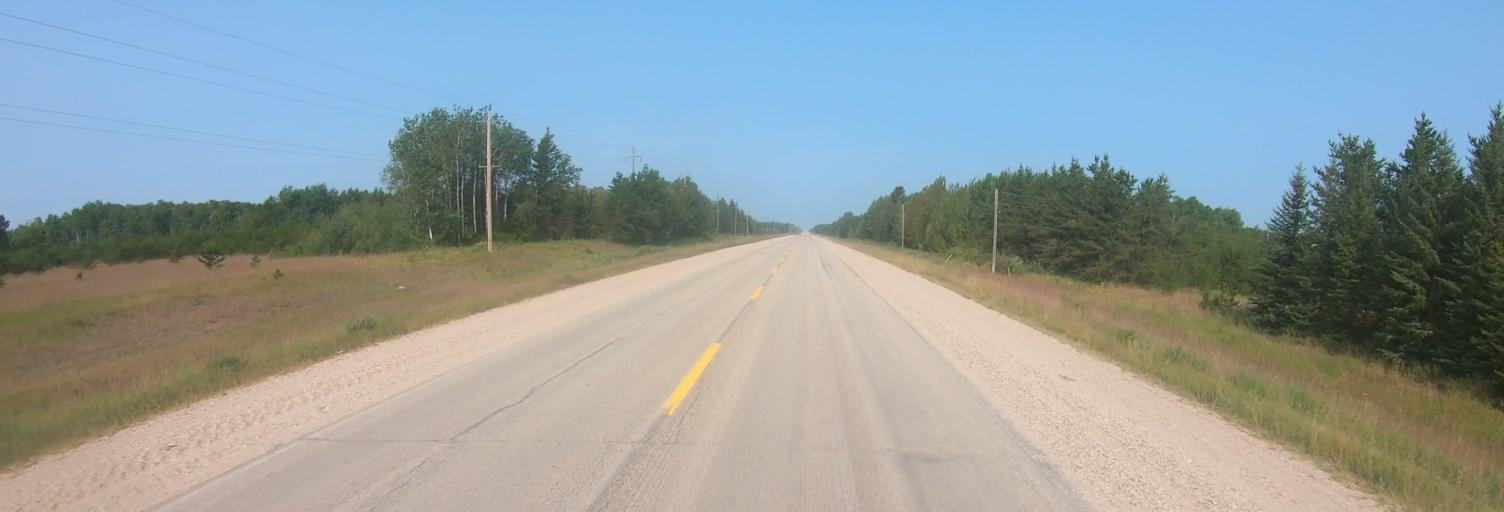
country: US
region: Minnesota
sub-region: Roseau County
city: Roseau
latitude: 49.0465
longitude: -95.7909
